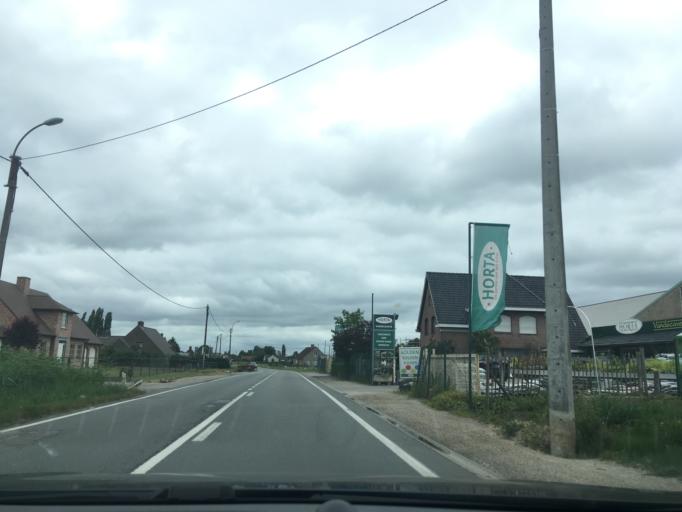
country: BE
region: Flanders
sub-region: Provincie West-Vlaanderen
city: Wingene
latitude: 51.0681
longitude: 3.2866
